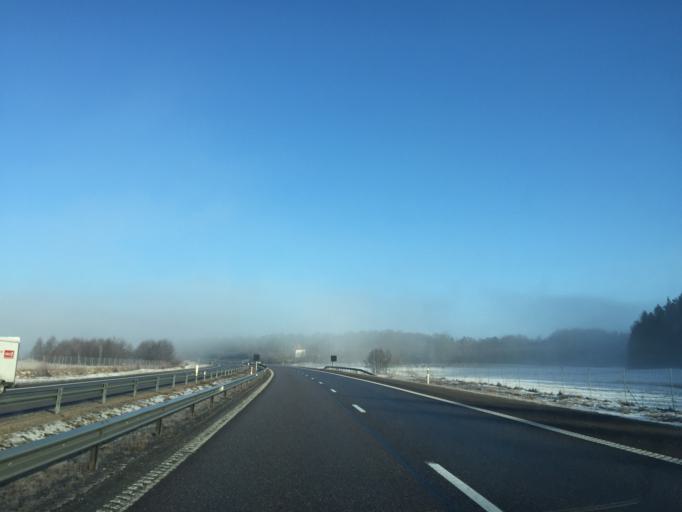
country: SE
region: Vaestra Goetaland
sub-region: Uddevalla Kommun
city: Uddevalla
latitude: 58.3120
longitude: 11.8591
